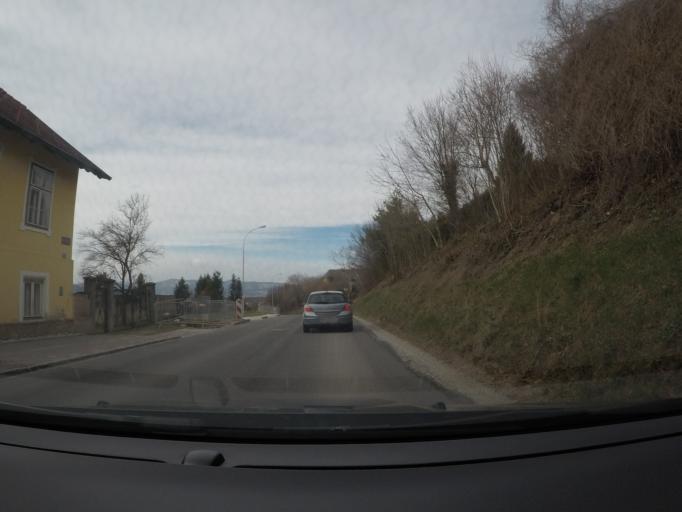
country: AT
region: Lower Austria
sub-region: Politischer Bezirk Neunkirchen
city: Pitten
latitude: 47.7244
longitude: 16.1789
